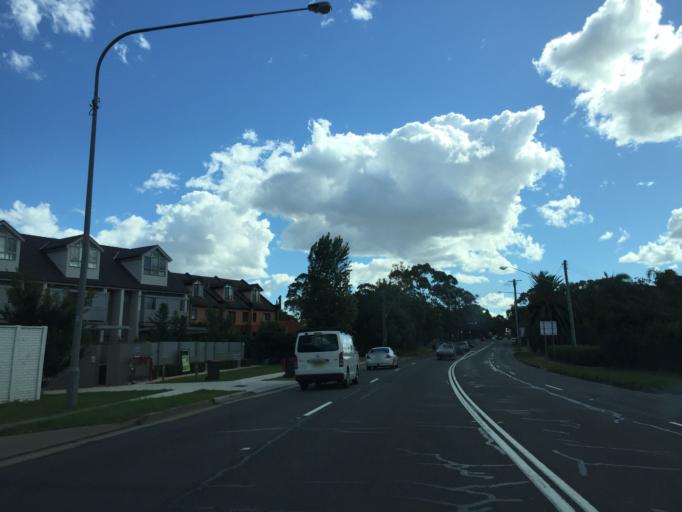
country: AU
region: New South Wales
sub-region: Parramatta
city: Telopea
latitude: -33.7868
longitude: 151.0306
